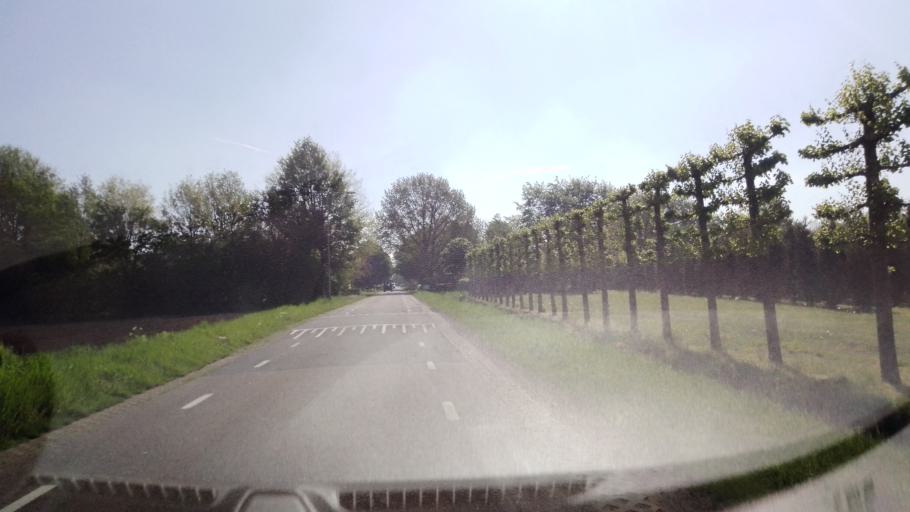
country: NL
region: Limburg
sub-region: Gemeente Peel en Maas
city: Maasbree
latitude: 51.4257
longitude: 6.0274
